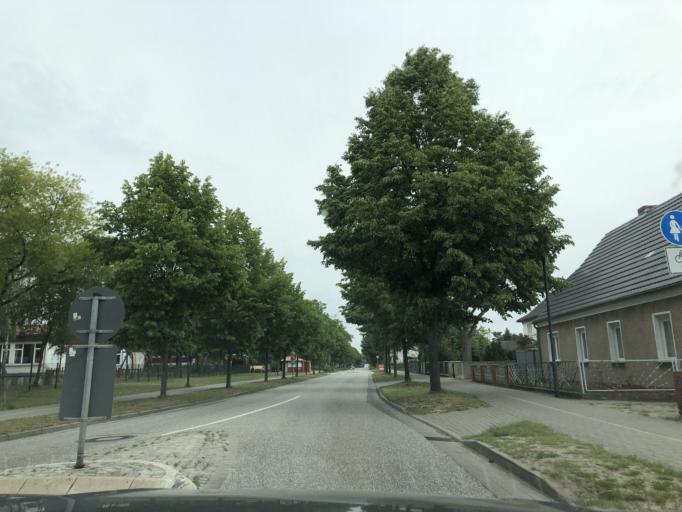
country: DE
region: Brandenburg
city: Plattenburg
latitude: 52.9115
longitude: 12.0854
